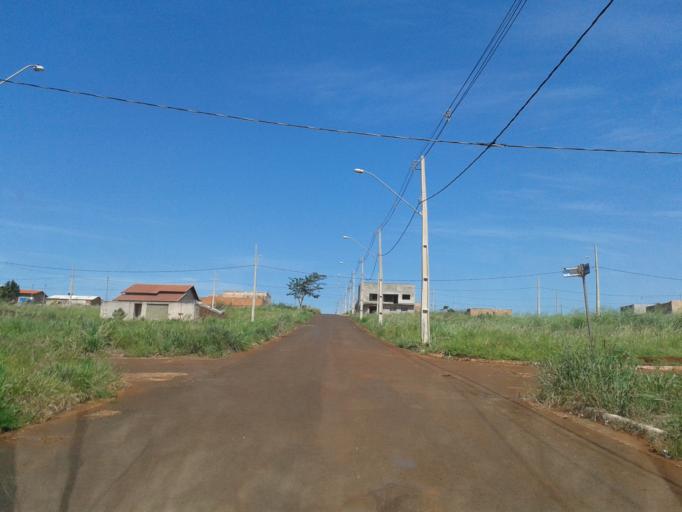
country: BR
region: Goias
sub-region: Itumbiara
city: Itumbiara
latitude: -18.4245
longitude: -49.1838
